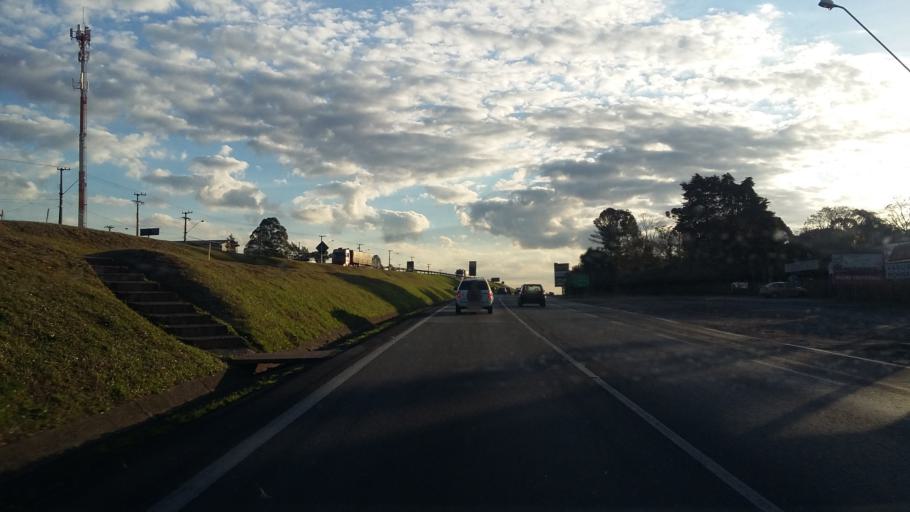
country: BR
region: Parana
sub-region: Campo Largo
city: Campo Largo
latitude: -25.4471
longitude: -49.4760
